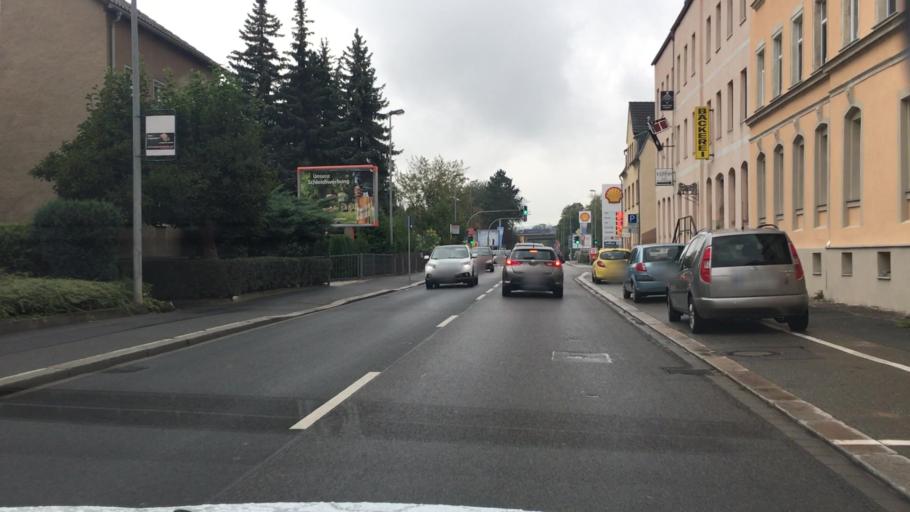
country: DE
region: Saxony
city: Chemnitz
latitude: 50.8702
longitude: 12.9104
